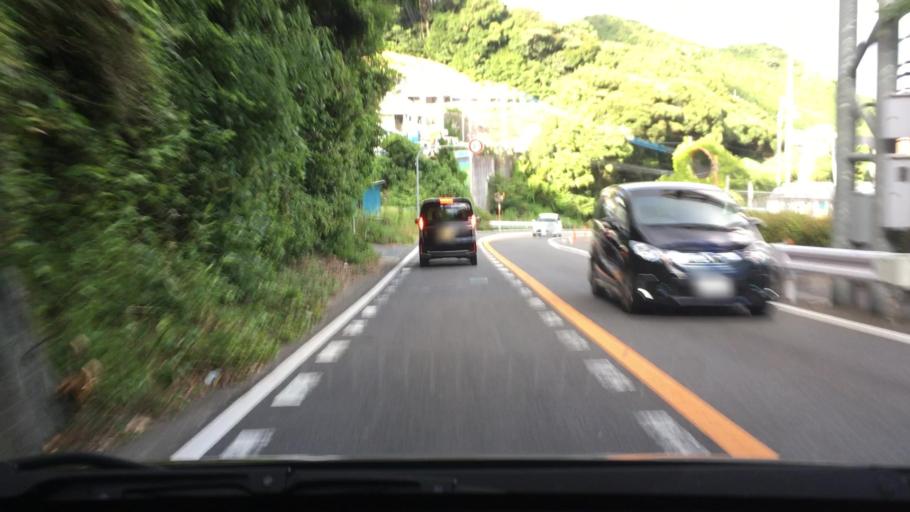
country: JP
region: Nagasaki
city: Togitsu
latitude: 32.8091
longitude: 129.8151
